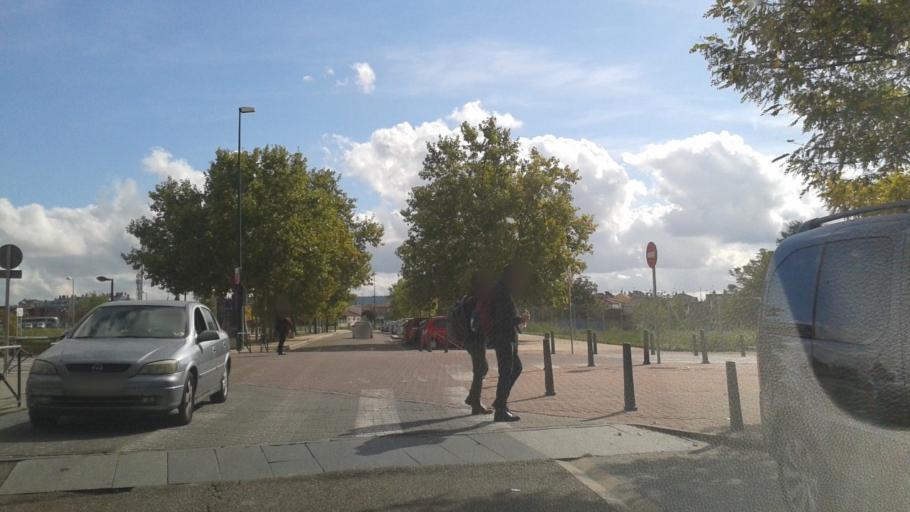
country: ES
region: Castille and Leon
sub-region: Provincia de Valladolid
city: Valladolid
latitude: 41.6615
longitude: -4.7079
